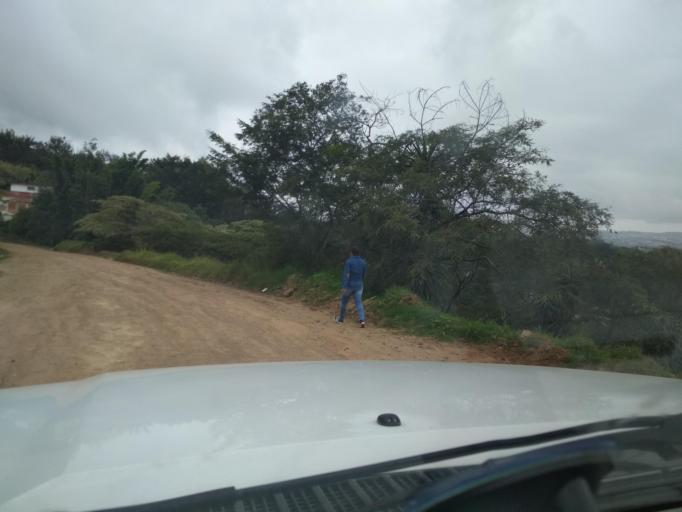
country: MX
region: Veracruz
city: El Castillo
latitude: 19.5448
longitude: -96.8319
